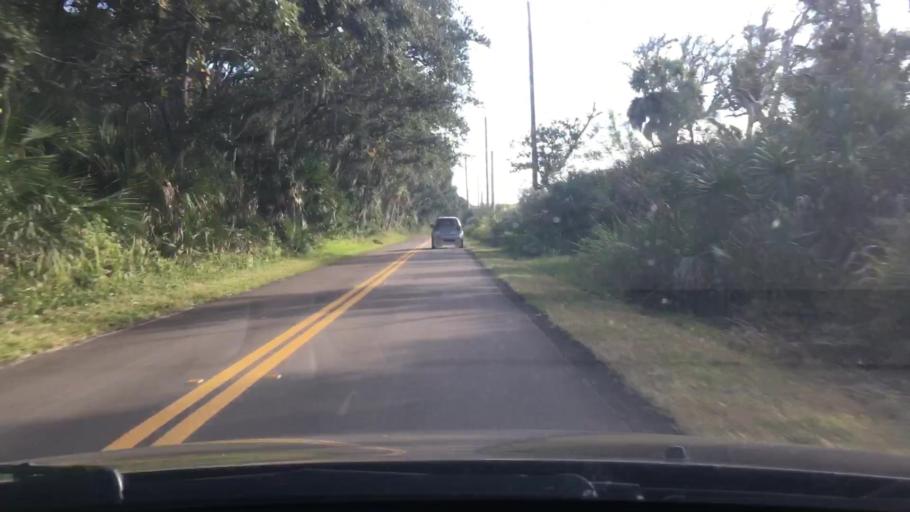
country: US
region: Florida
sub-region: Volusia County
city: Ormond-by-the-Sea
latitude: 29.3947
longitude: -81.0918
